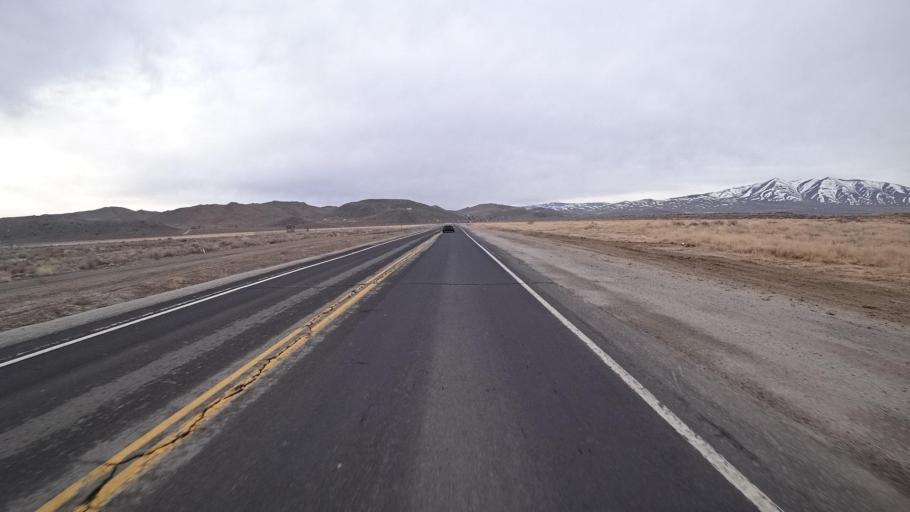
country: US
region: Nevada
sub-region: Washoe County
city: Lemmon Valley
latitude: 39.6590
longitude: -119.8270
